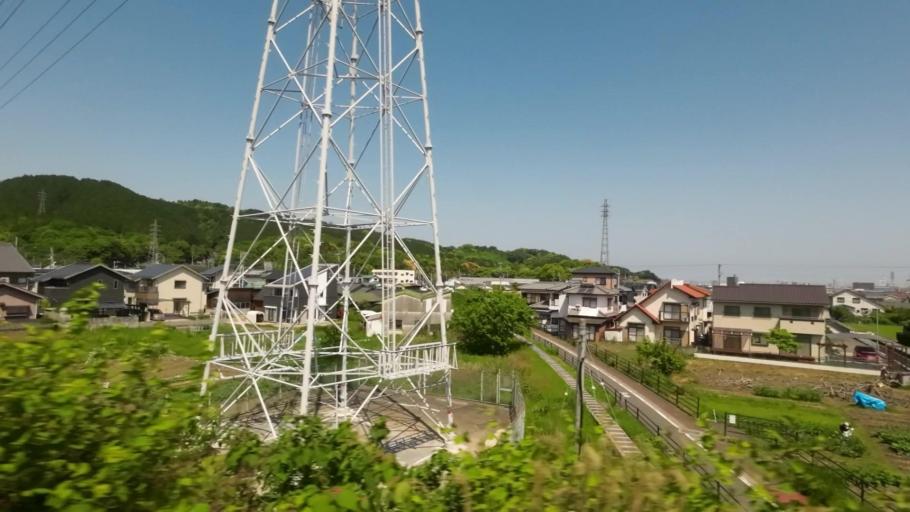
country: JP
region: Ehime
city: Niihama
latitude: 33.9396
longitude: 133.2853
